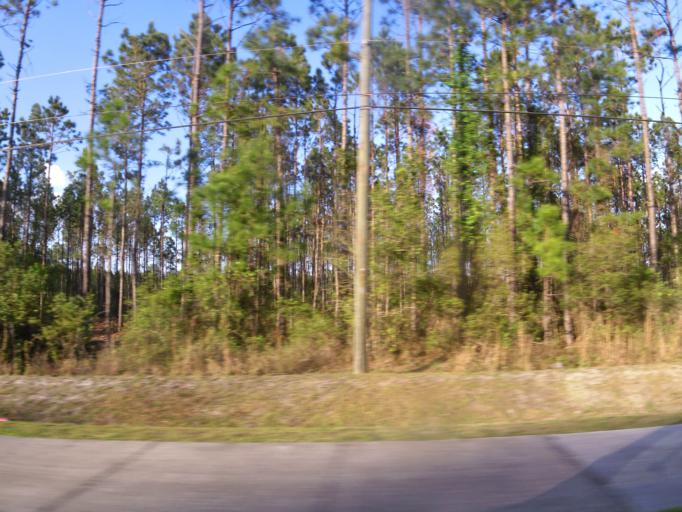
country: US
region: Florida
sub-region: Saint Johns County
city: Fruit Cove
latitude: 30.0687
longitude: -81.5079
